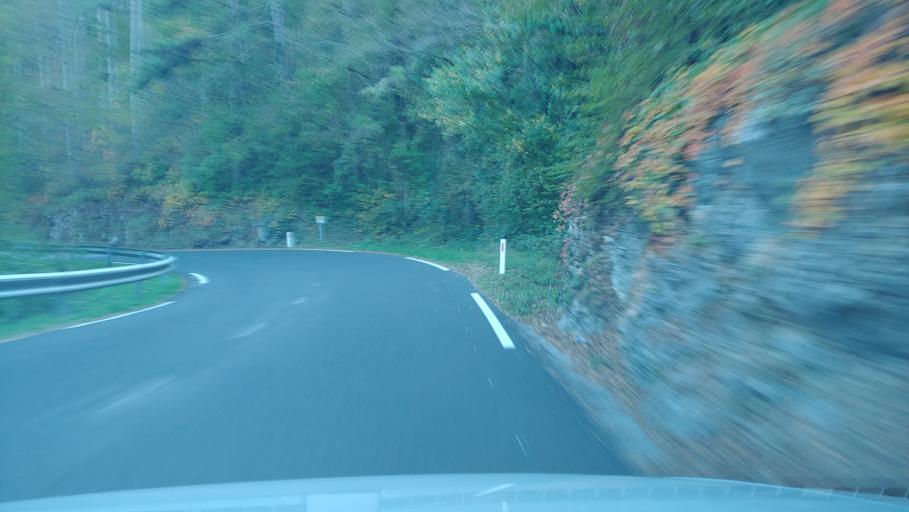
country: SI
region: Ajdovscina
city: Ajdovscina
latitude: 45.8073
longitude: 13.8595
